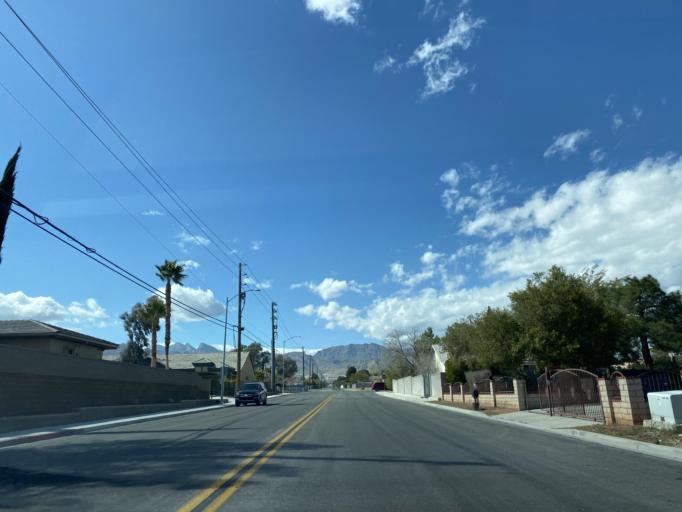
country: US
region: Nevada
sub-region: Clark County
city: Summerlin South
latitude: 36.2556
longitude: -115.2775
